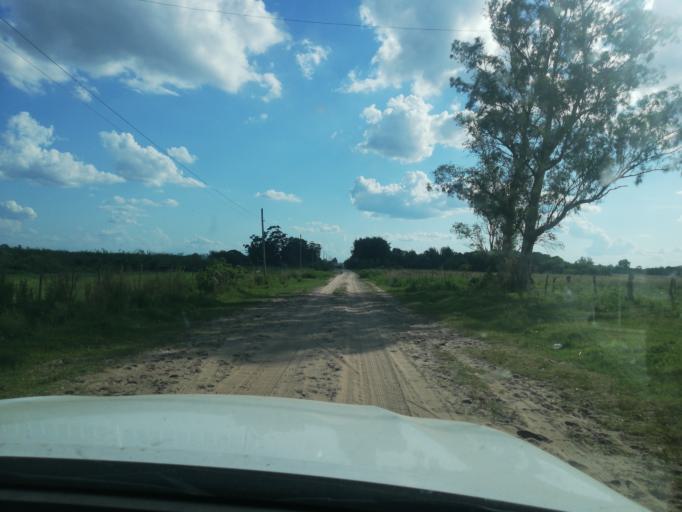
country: AR
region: Corrientes
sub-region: Departamento de San Miguel
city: San Miguel
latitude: -27.9931
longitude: -57.5764
